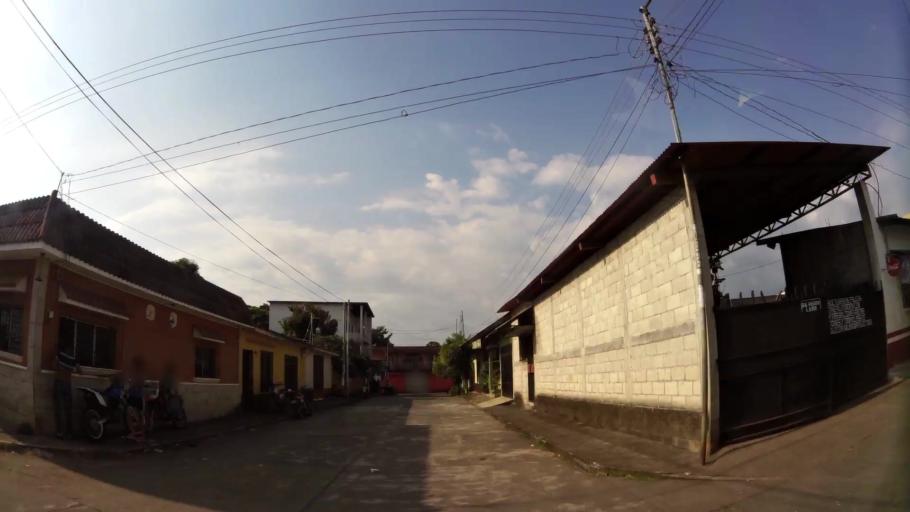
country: GT
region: Retalhuleu
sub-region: Municipio de Retalhuleu
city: Retalhuleu
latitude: 14.5301
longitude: -91.6908
